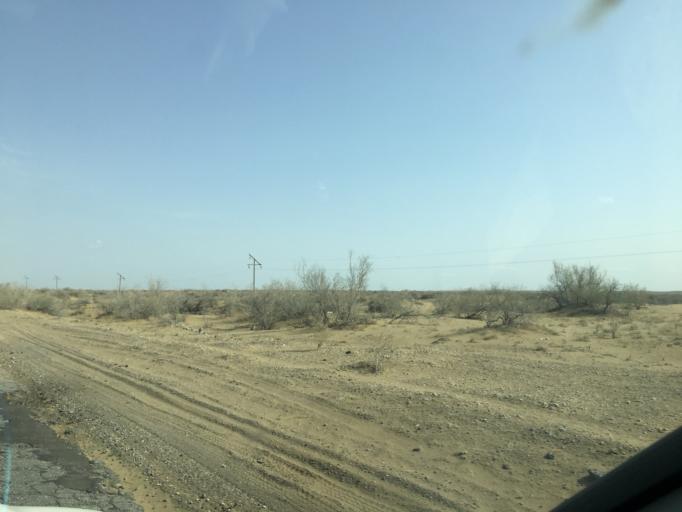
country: TM
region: Lebap
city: Farap
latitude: 39.3284
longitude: 63.3350
